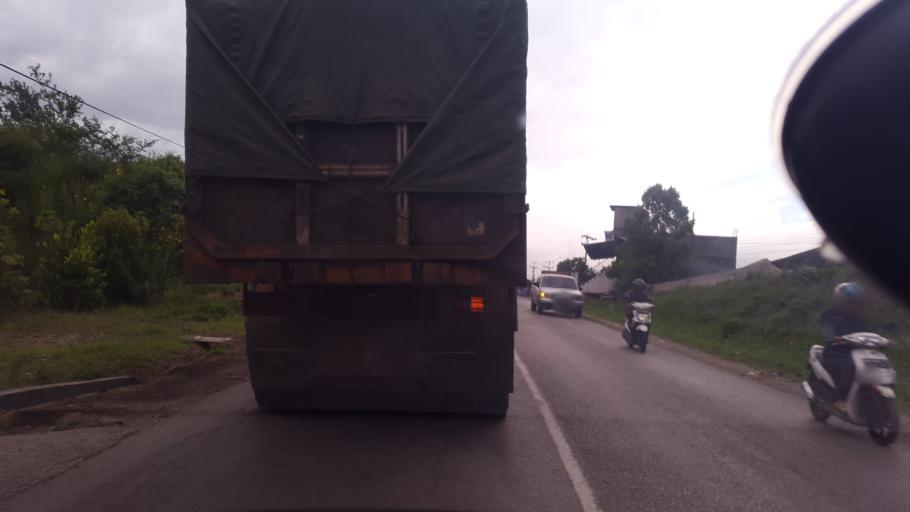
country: ID
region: West Sumatra
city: Gunung Talang
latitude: -0.9075
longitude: 100.6427
